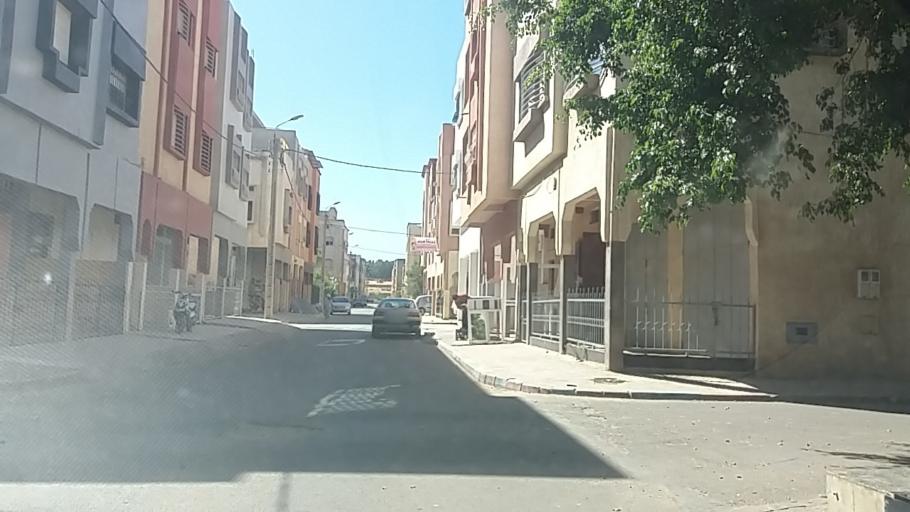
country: MA
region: Gharb-Chrarda-Beni Hssen
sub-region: Kenitra Province
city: Kenitra
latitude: 34.2384
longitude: -6.6173
